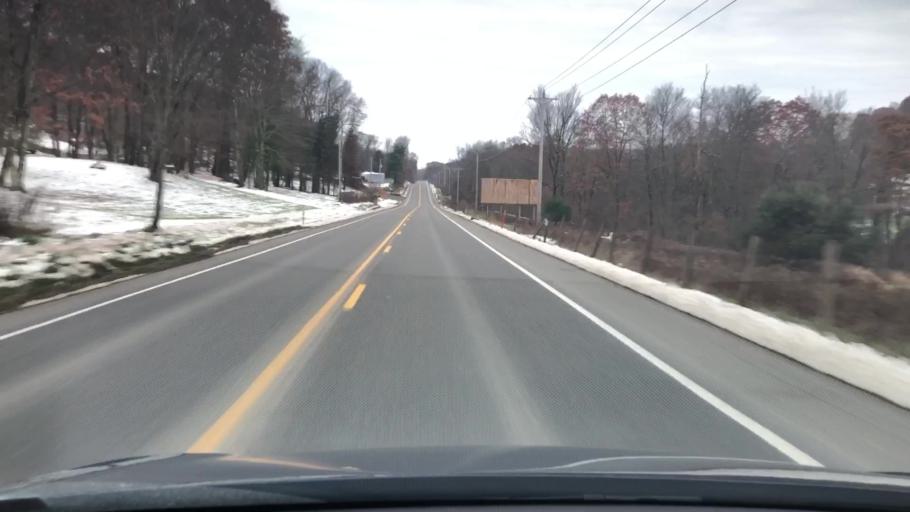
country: US
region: Pennsylvania
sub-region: Jefferson County
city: Brookville
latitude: 41.0621
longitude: -79.2447
